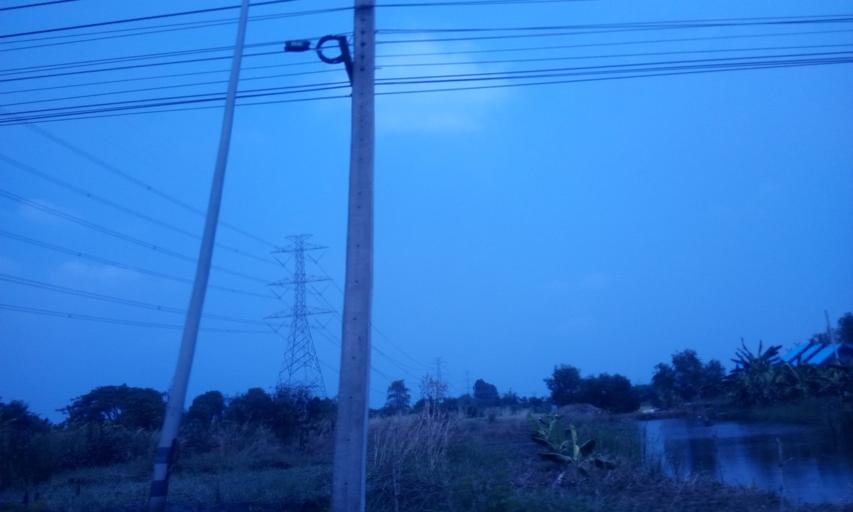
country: TH
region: Pathum Thani
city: Ban Lam Luk Ka
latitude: 13.9594
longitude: 100.8789
